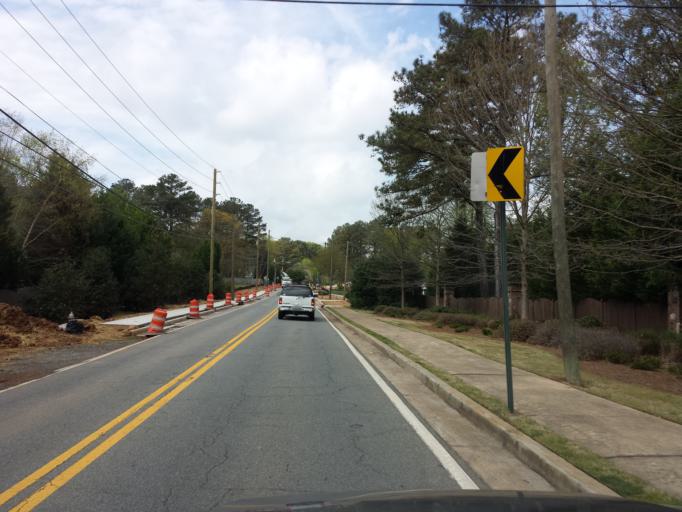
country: US
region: Georgia
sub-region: Cherokee County
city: Woodstock
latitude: 34.0314
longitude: -84.4966
